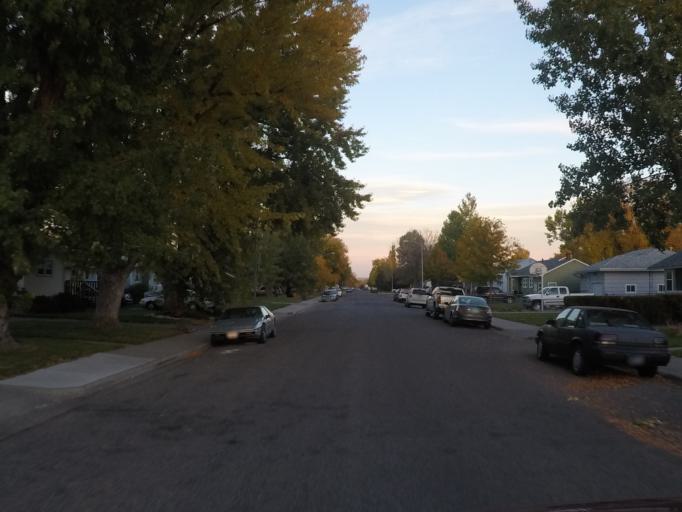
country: US
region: Montana
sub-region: Yellowstone County
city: Billings
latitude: 45.7879
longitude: -108.5454
